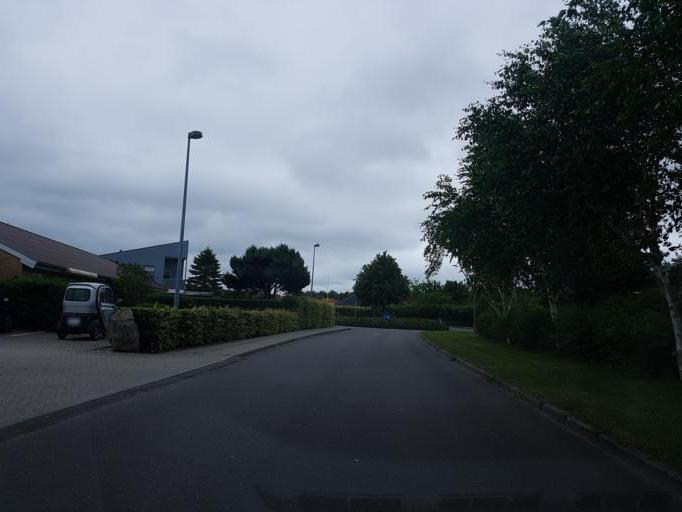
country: DK
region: South Denmark
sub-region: Varde Kommune
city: Varde
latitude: 55.6354
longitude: 8.4822
